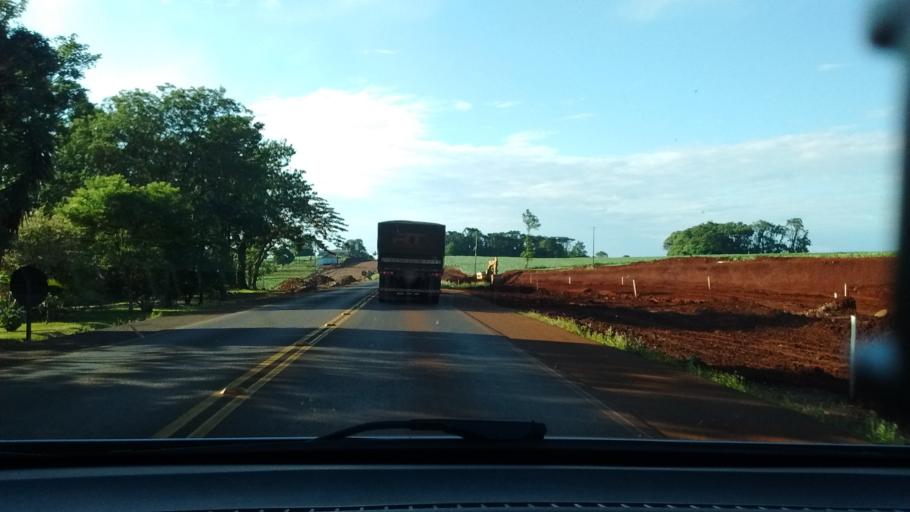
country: BR
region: Parana
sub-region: Cascavel
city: Cascavel
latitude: -25.1745
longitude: -53.6033
